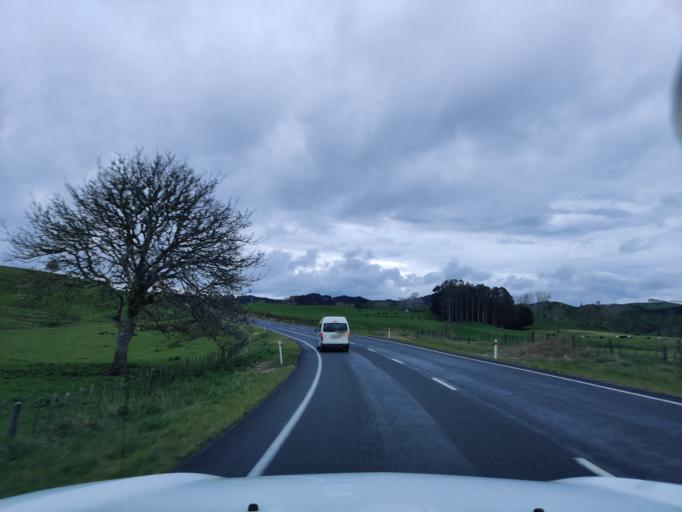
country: NZ
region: Waikato
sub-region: Otorohanga District
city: Otorohanga
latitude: -38.4568
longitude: 175.1675
